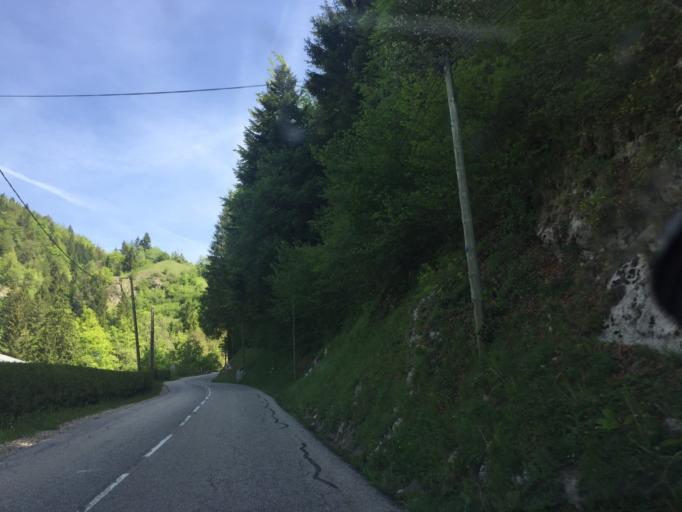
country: FR
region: Rhone-Alpes
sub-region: Departement de l'Isere
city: Saint-Vincent-de-Mercuze
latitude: 45.4262
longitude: 5.8668
